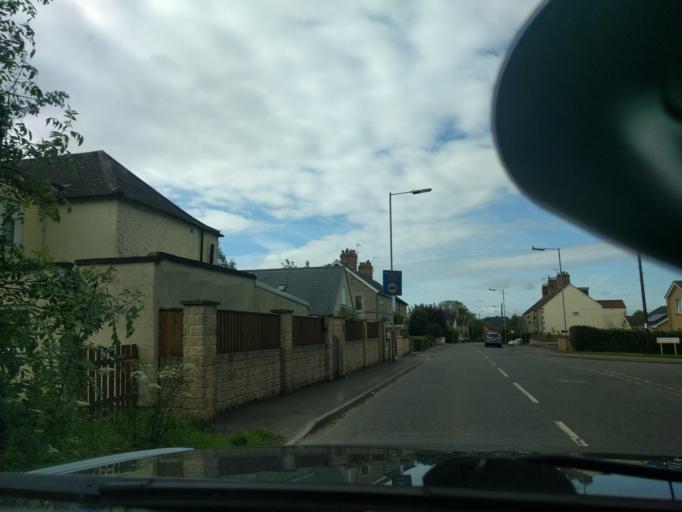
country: GB
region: England
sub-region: Wiltshire
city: Calne
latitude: 51.4462
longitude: -1.9960
